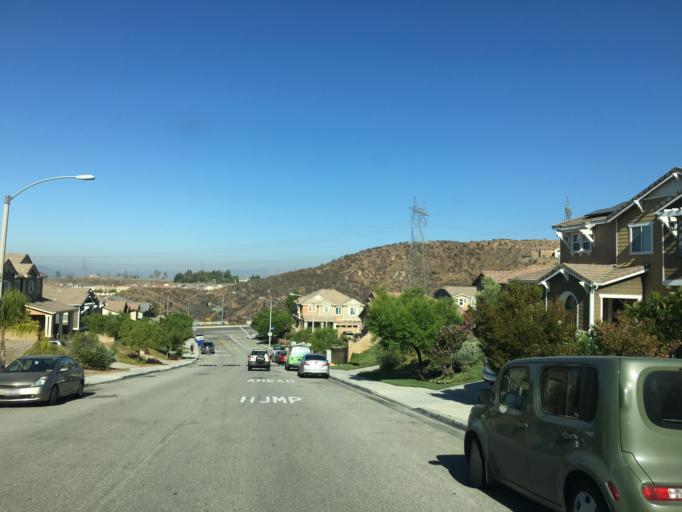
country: US
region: California
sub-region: Los Angeles County
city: Santa Clarita
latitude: 34.4386
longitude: -118.4935
